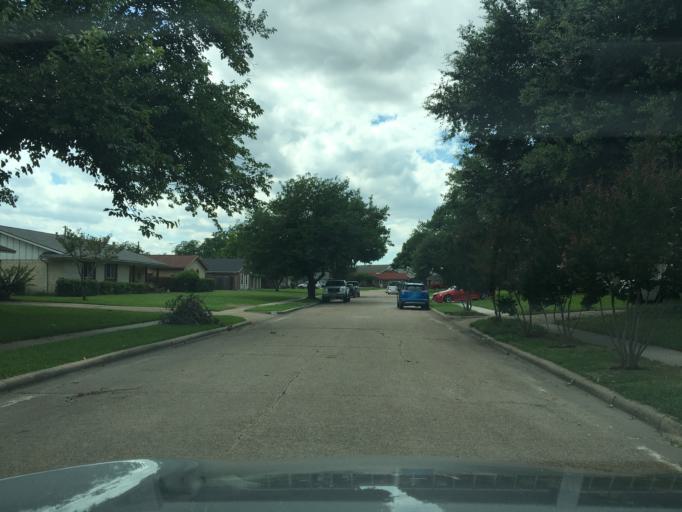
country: US
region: Texas
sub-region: Dallas County
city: Richardson
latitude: 32.9466
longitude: -96.7071
